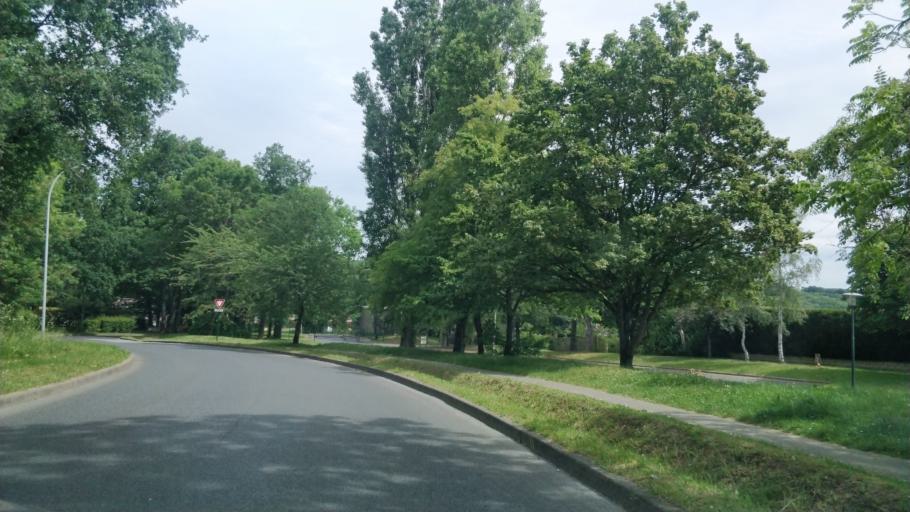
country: FR
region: Ile-de-France
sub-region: Departement de l'Essonne
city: Limours
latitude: 48.6412
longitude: 2.0807
